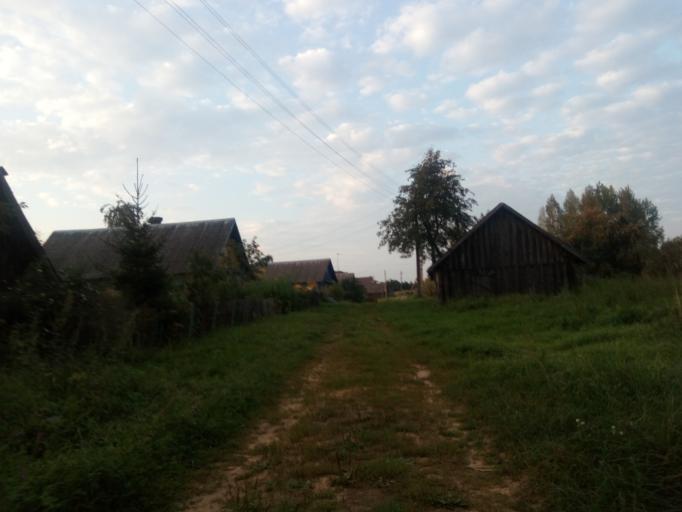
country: BY
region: Vitebsk
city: Dzisna
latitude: 55.6590
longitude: 28.3311
